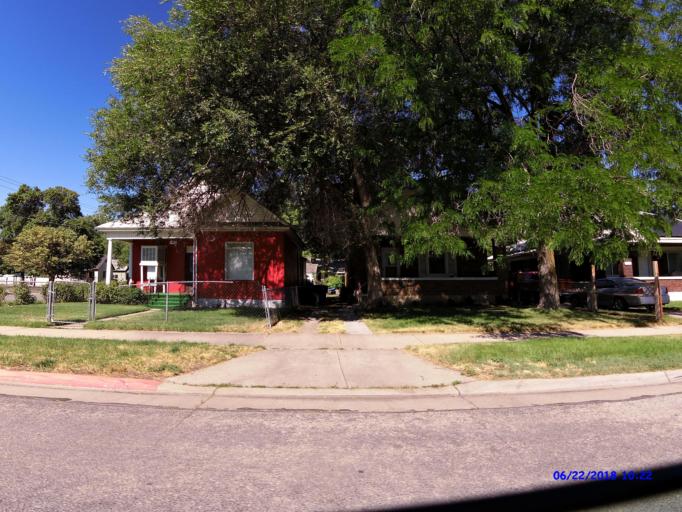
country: US
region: Utah
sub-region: Weber County
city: Ogden
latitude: 41.2126
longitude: -111.9736
